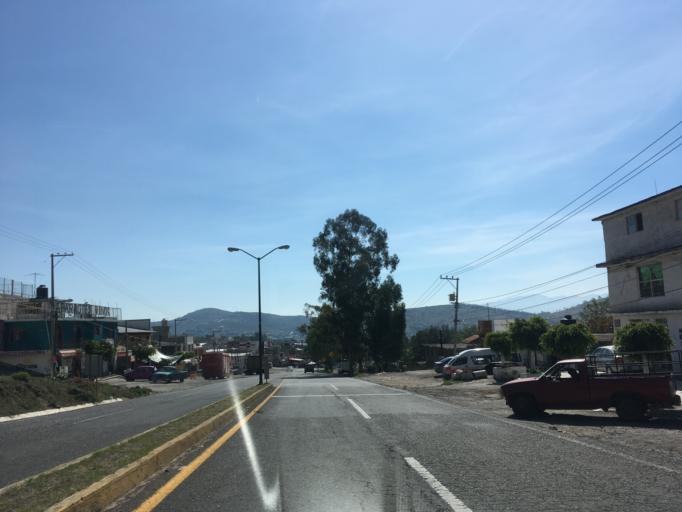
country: MX
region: Michoacan
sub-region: Morelia
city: Puerto de Buenavista (Lazaro Cardenas)
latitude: 19.6865
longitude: -101.1291
